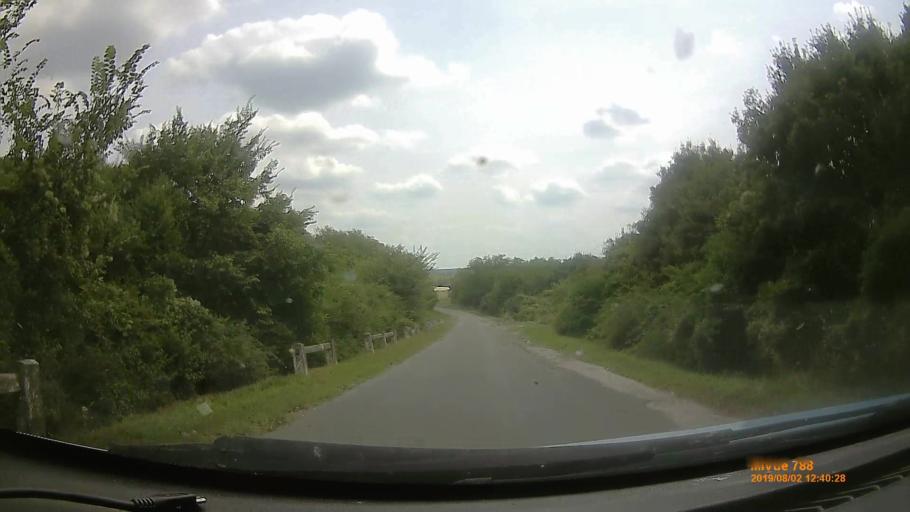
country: HU
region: Baranya
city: Buekkoesd
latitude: 46.0857
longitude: 17.9682
